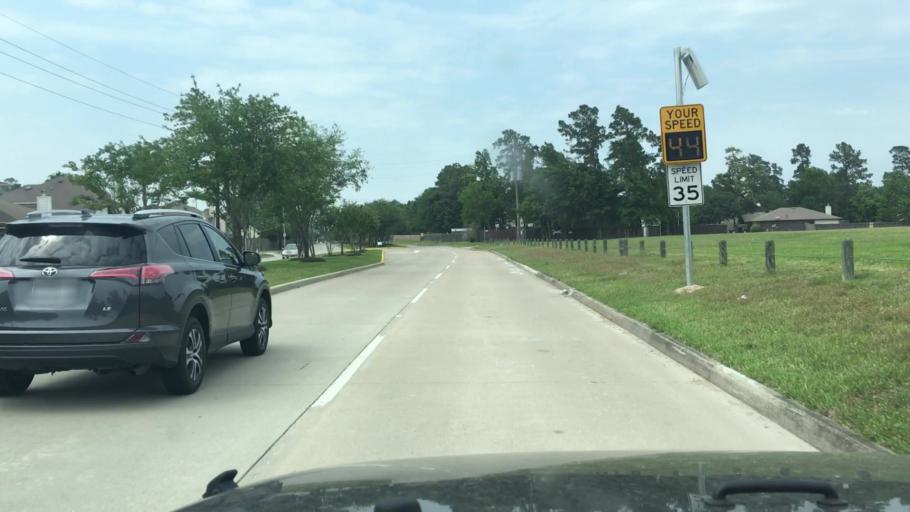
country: US
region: Texas
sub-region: Harris County
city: Atascocita
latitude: 29.9638
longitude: -95.2102
